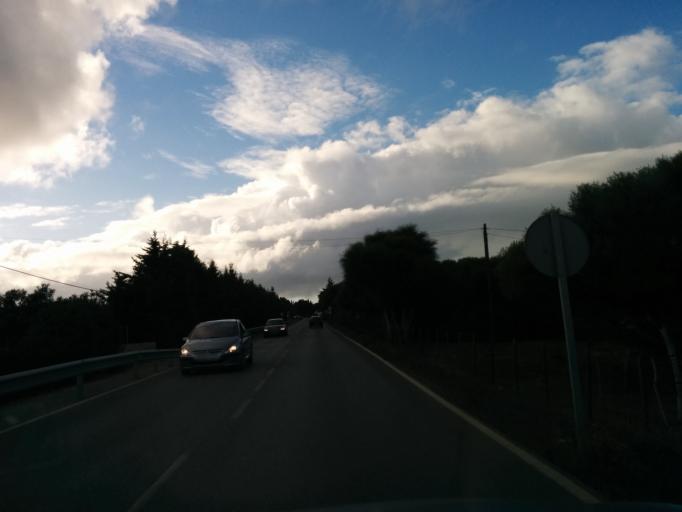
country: ES
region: Andalusia
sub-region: Provincia de Cadiz
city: Vejer de la Frontera
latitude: 36.1981
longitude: -6.0316
